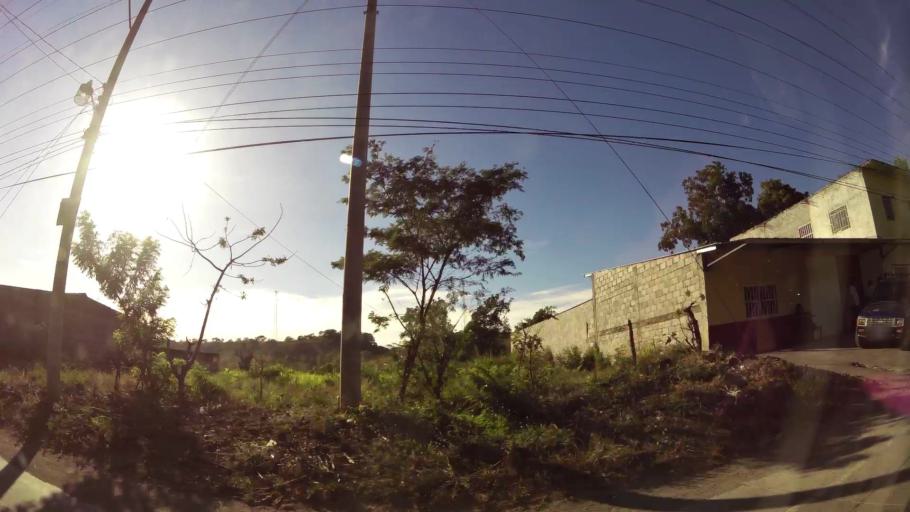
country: SV
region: Santa Ana
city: Metapan
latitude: 14.2984
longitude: -89.4631
